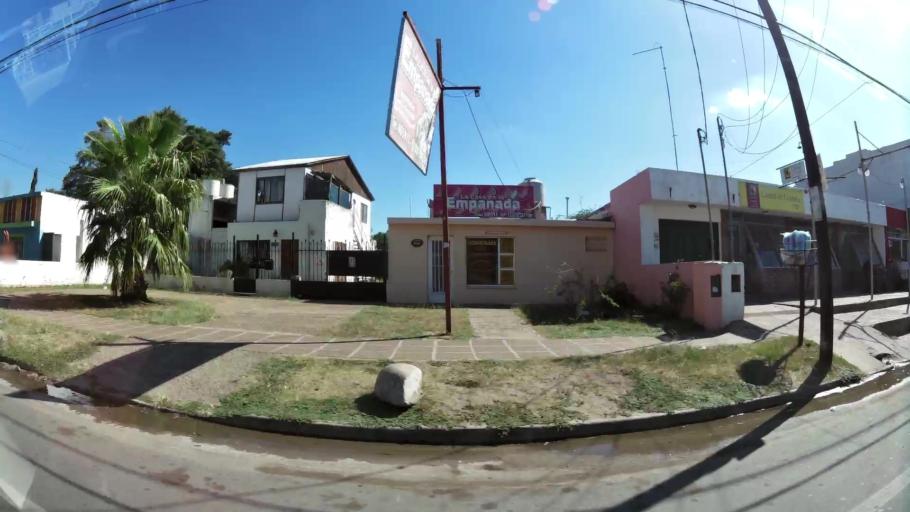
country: AR
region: Cordoba
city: Villa Allende
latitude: -31.3304
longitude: -64.2648
